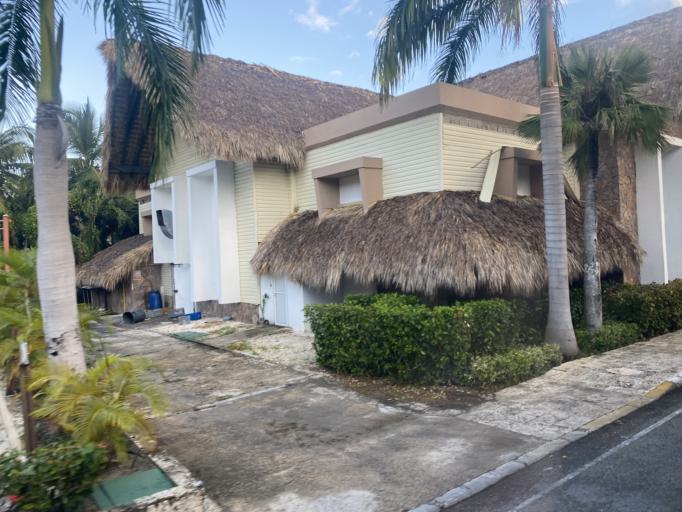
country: DO
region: San Juan
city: Punta Cana
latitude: 18.7279
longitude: -68.4700
